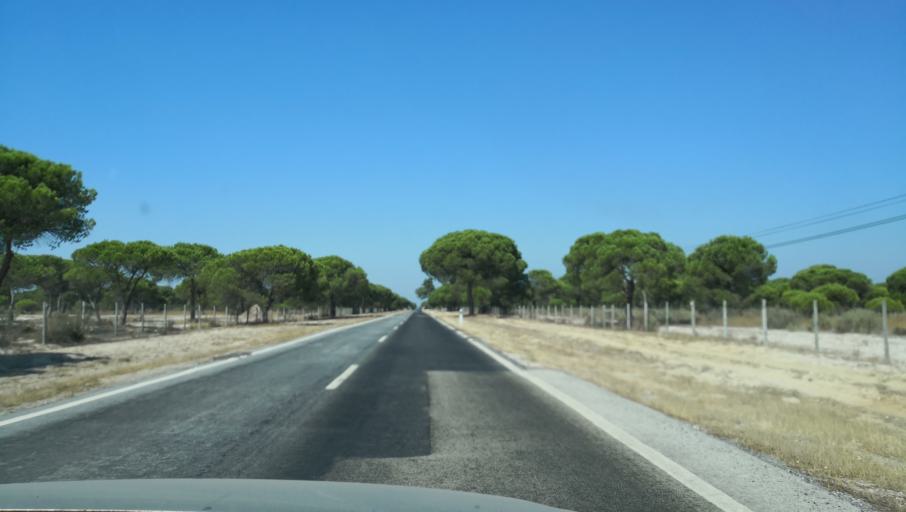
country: PT
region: Setubal
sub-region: Alcacer do Sal
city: Alcacer do Sal
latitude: 38.3839
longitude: -8.5625
